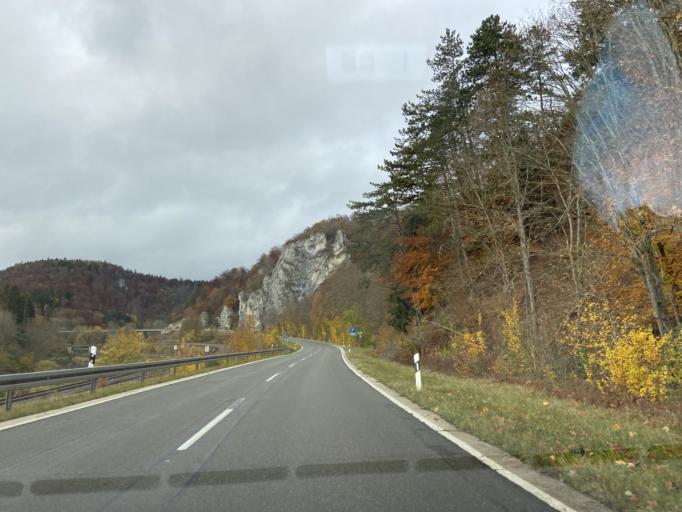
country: DE
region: Baden-Wuerttemberg
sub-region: Tuebingen Region
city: Inzigkofen
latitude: 48.0773
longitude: 9.1585
